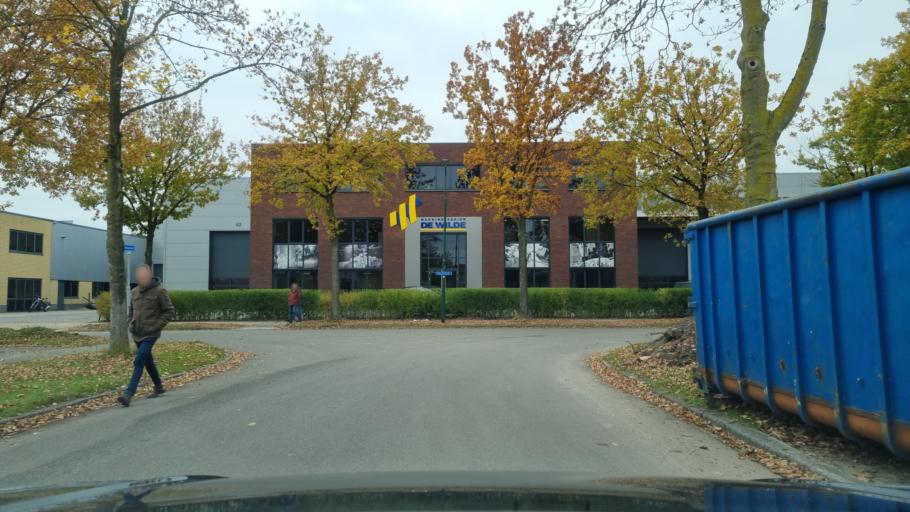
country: NL
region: Utrecht
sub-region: Gemeente Veenendaal
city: Veenendaal
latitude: 52.0402
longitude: 5.5455
